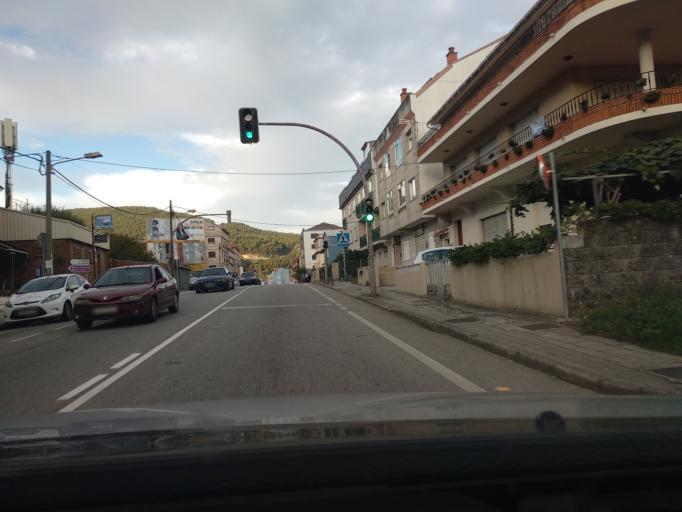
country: ES
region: Galicia
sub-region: Provincia de Pontevedra
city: Vigo
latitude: 42.2858
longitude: -8.6834
